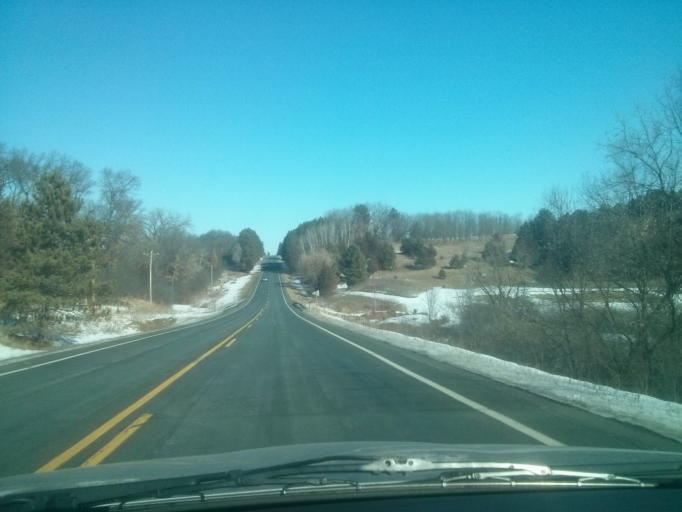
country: US
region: Minnesota
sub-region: Washington County
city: Bayport
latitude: 45.0422
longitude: -92.7411
